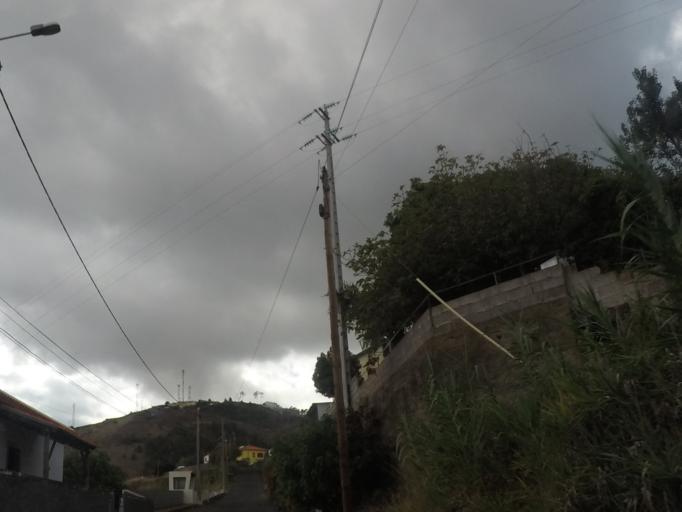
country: PT
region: Madeira
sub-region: Santa Cruz
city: Camacha
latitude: 32.6636
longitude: -16.8265
